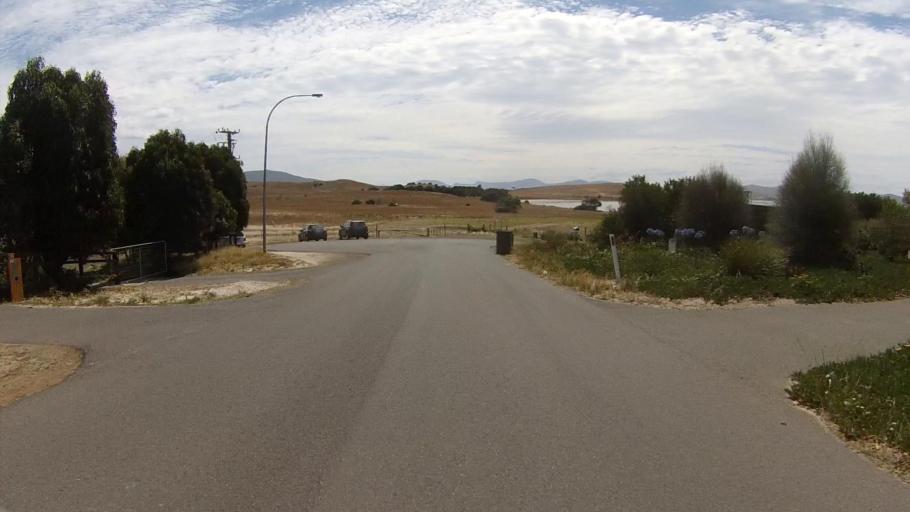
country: AU
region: Tasmania
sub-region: Kingborough
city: Taroona
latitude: -42.9832
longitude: 147.4055
